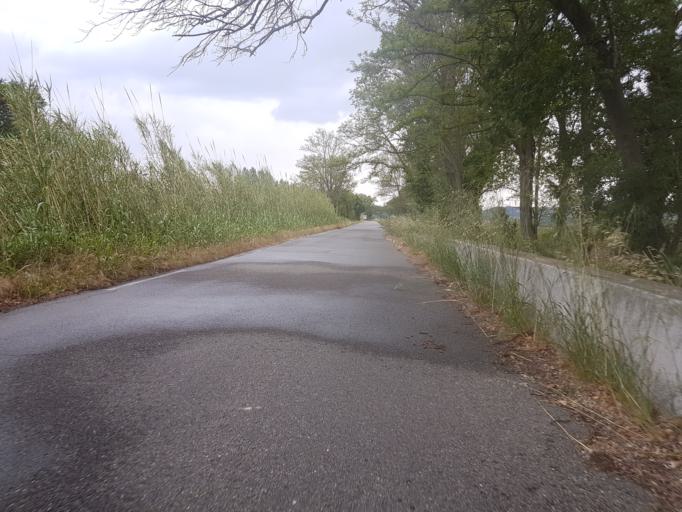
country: FR
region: Provence-Alpes-Cote d'Azur
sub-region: Departement du Vaucluse
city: Avignon
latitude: 43.9608
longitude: 4.8124
